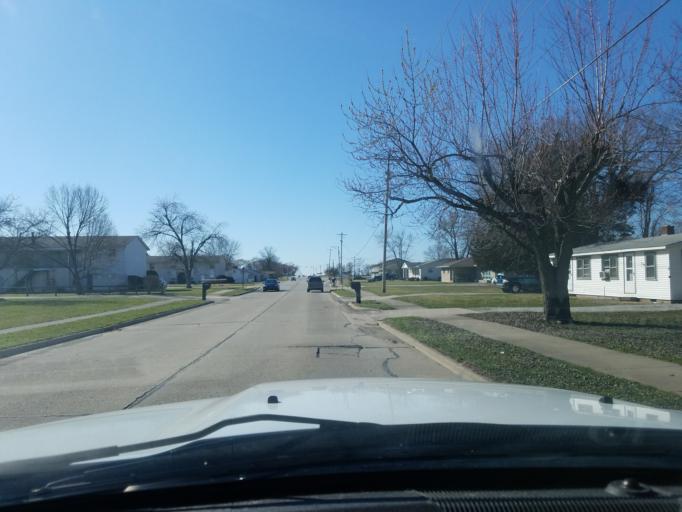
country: US
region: Indiana
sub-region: Shelby County
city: Shelbyville
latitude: 39.5046
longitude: -85.7981
